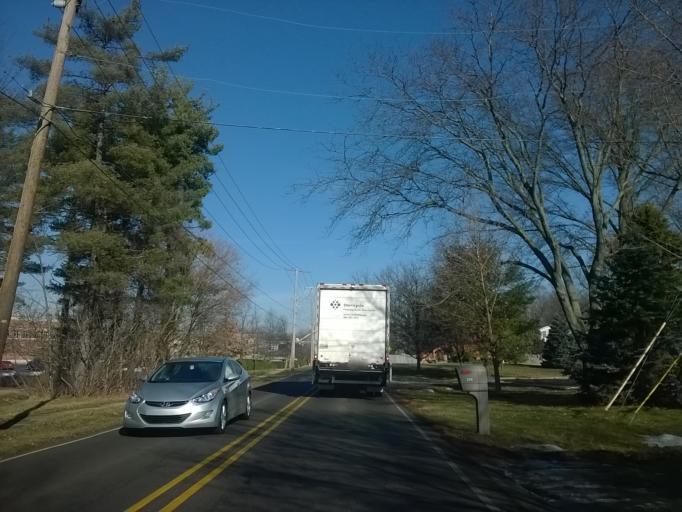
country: US
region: Indiana
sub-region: Hamilton County
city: Carmel
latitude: 39.9796
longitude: -86.1410
